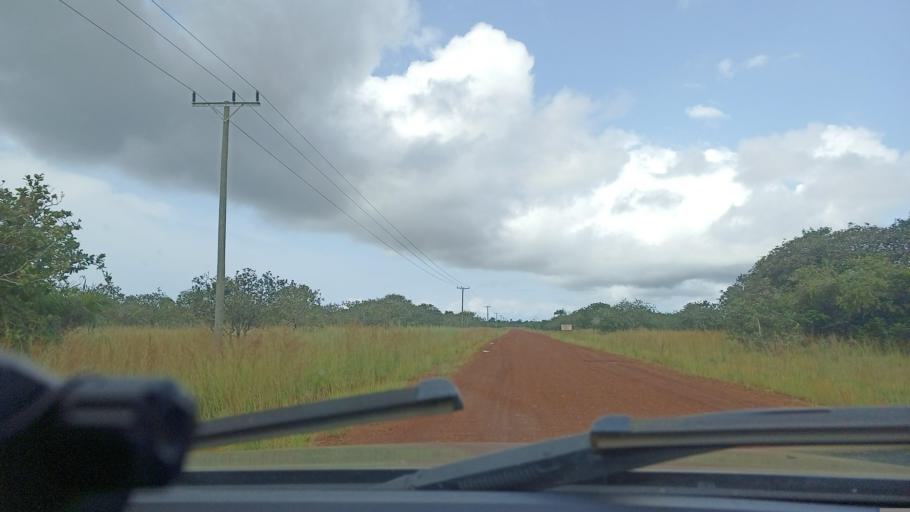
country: LR
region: Grand Cape Mount
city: Robertsport
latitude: 6.6916
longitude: -11.2731
